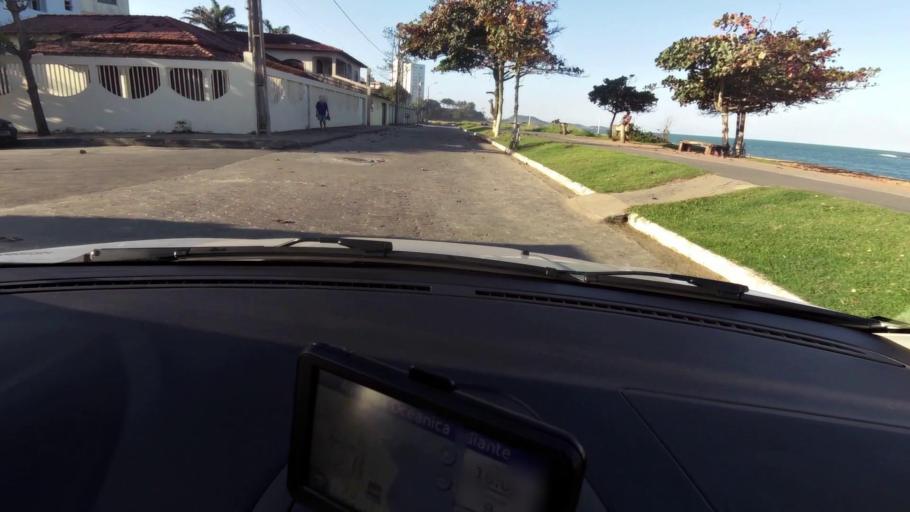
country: BR
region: Espirito Santo
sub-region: Guarapari
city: Guarapari
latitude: -20.6829
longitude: -40.5055
